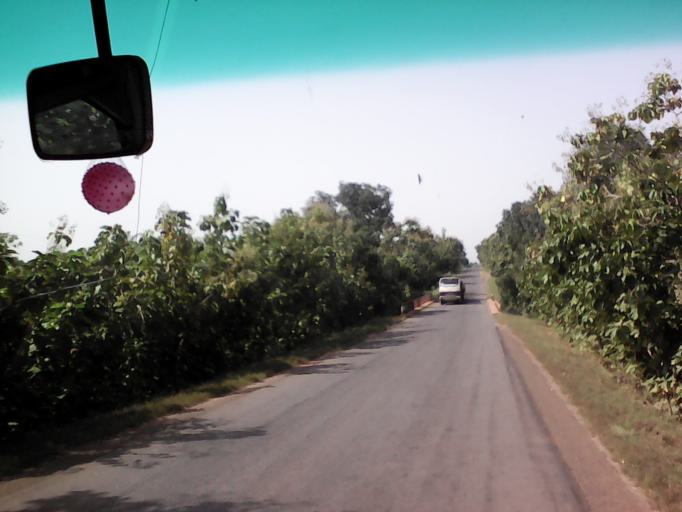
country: TG
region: Centrale
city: Sokode
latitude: 8.9072
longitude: 1.0967
